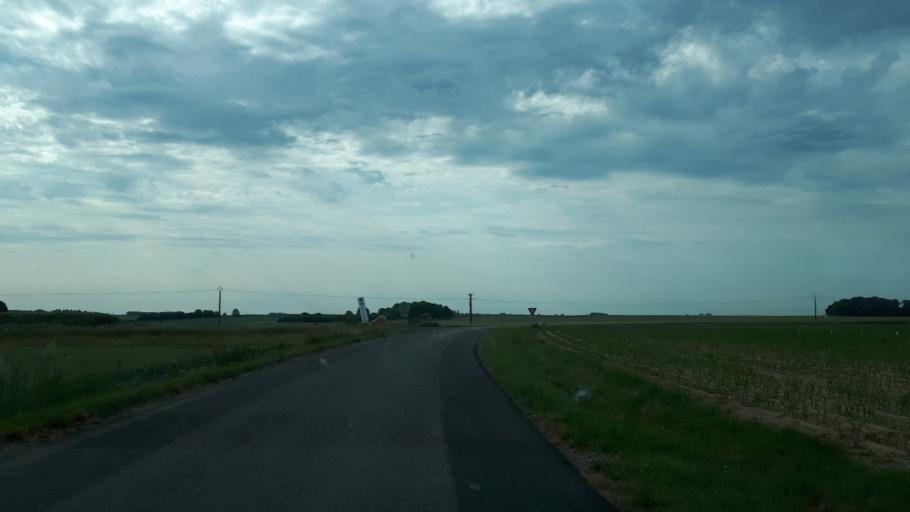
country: FR
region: Centre
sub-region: Departement du Loir-et-Cher
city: Saint-Amand-Longpre
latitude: 47.7157
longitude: 1.0124
